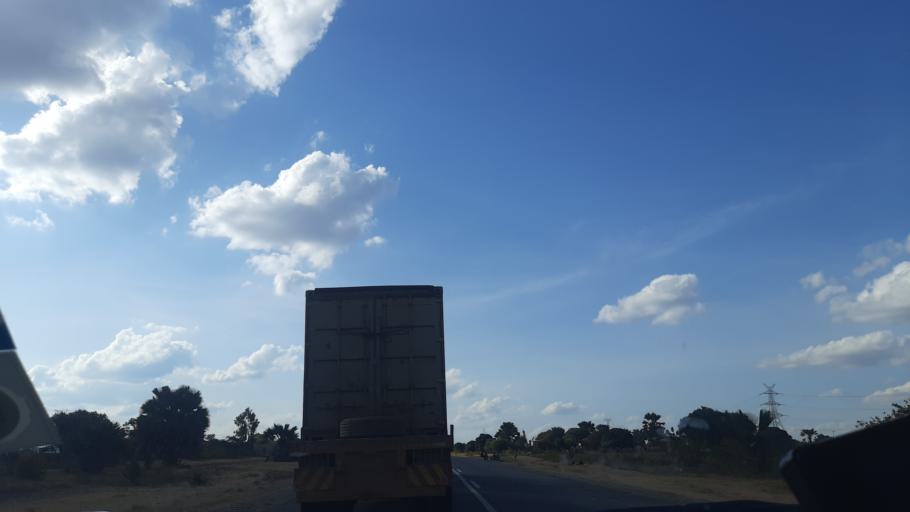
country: TZ
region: Singida
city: Ikungi
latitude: -5.0886
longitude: 34.7658
